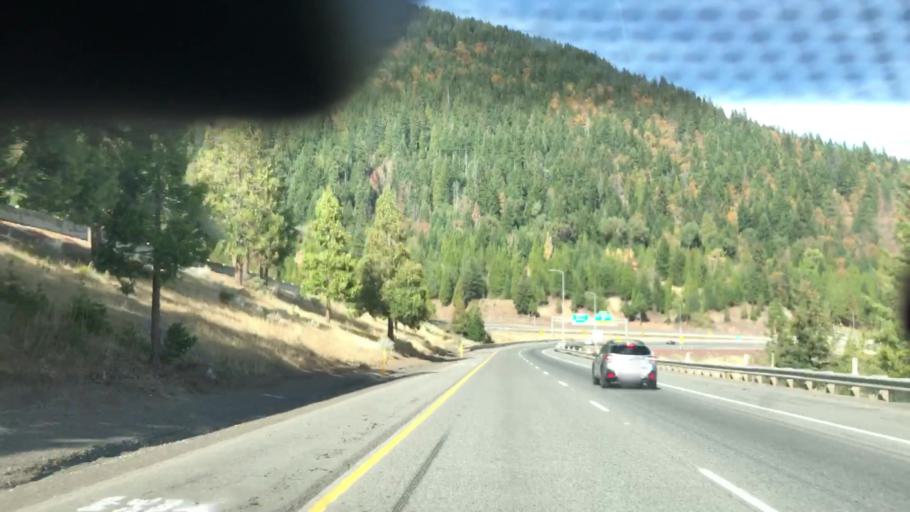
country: US
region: Oregon
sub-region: Jackson County
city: Ashland
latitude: 42.0715
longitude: -122.6043
